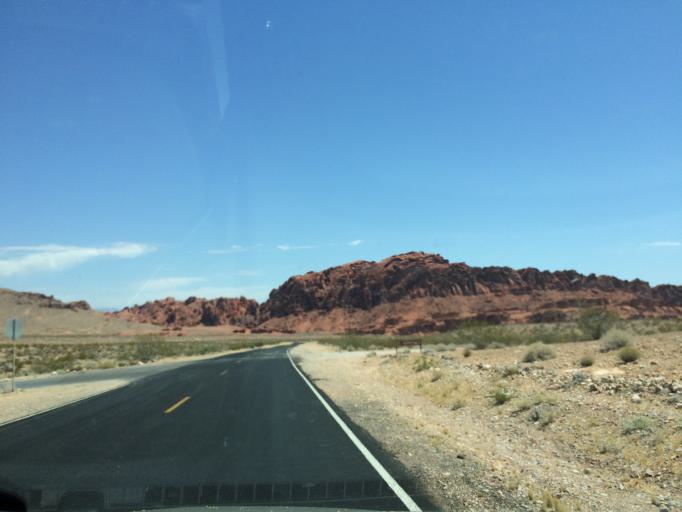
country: US
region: Nevada
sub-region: Clark County
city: Moapa Valley
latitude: 36.4212
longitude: -114.5443
